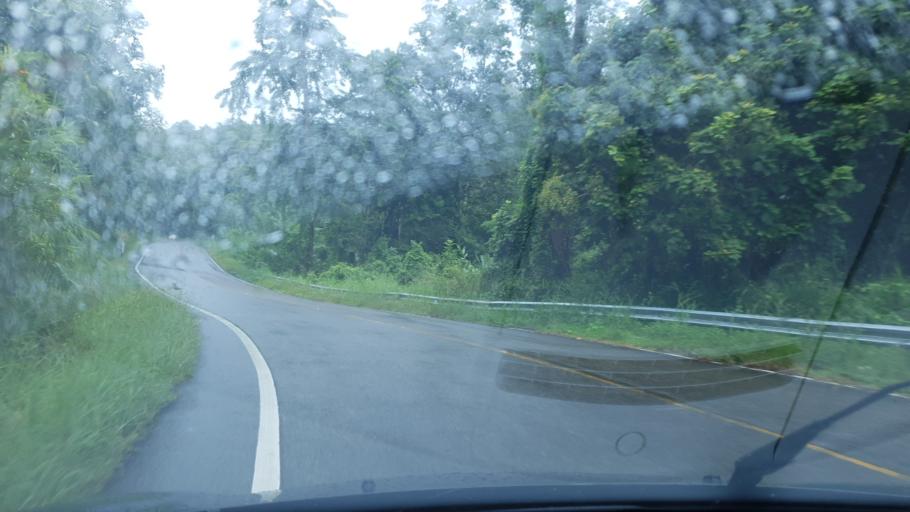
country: TH
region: Mae Hong Son
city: Mae La Noi
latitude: 18.5566
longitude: 97.9414
